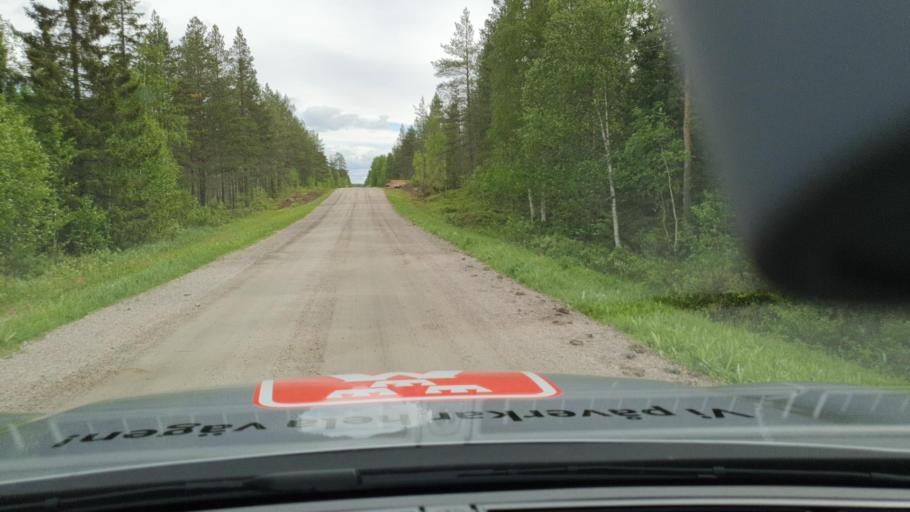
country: FI
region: Lapland
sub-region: Torniolaakso
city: Ylitornio
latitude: 65.9504
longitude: 23.5649
